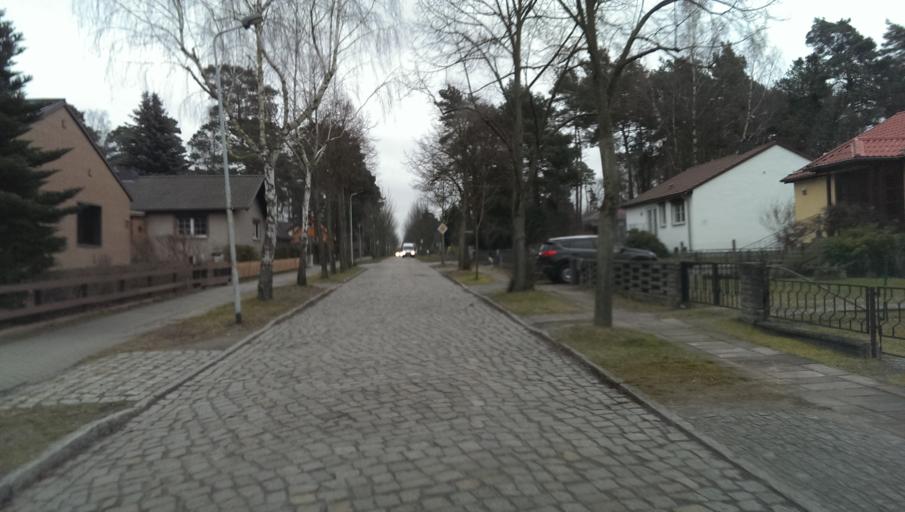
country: DE
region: Brandenburg
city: Rangsdorf
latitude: 52.3250
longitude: 13.3948
